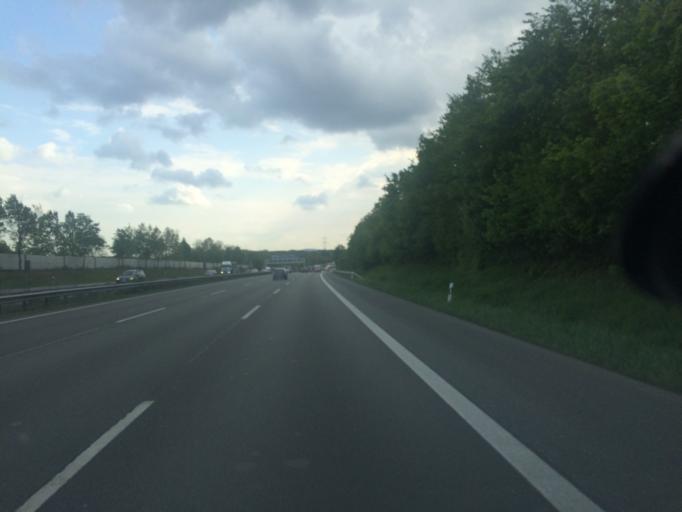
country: DE
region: North Rhine-Westphalia
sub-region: Regierungsbezirk Detmold
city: Leopoldshohe
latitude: 52.0560
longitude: 8.6583
